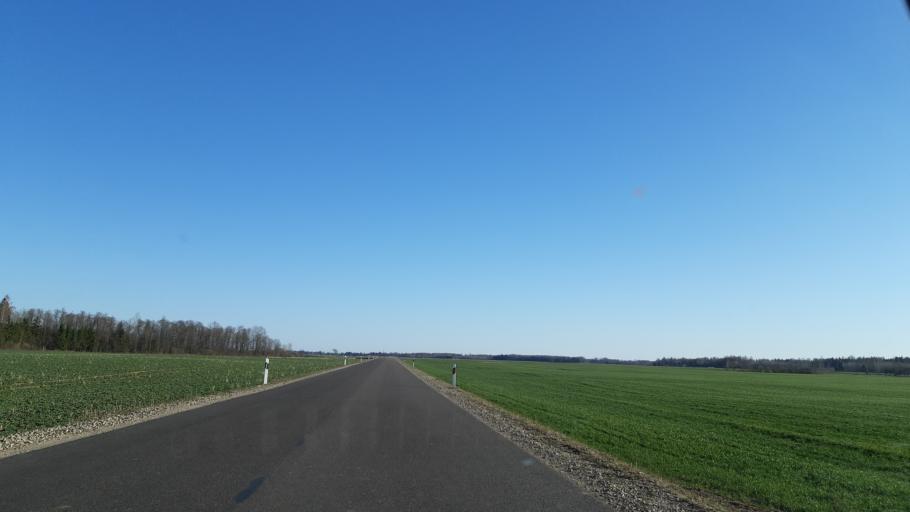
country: LT
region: Kauno apskritis
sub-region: Kaunas
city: Sargenai
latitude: 55.0258
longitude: 23.7610
